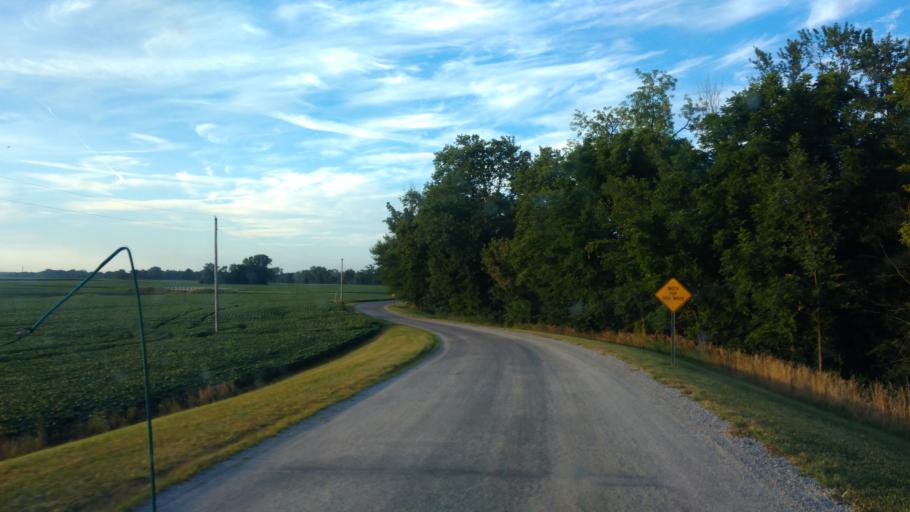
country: US
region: Indiana
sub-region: Adams County
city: Berne
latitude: 40.6439
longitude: -85.0300
